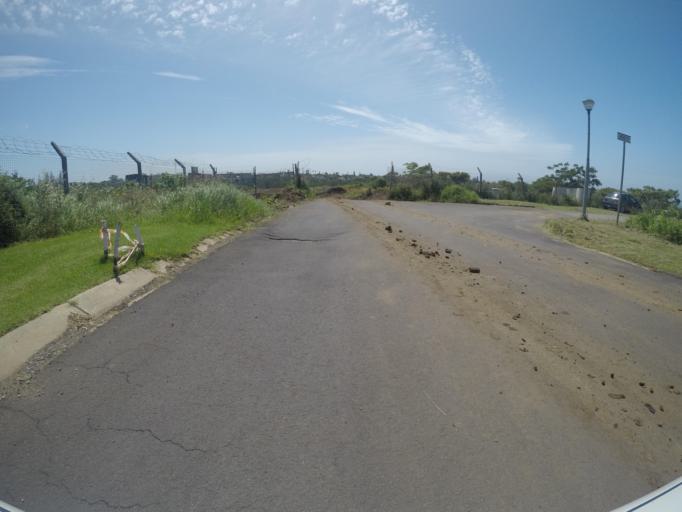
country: ZA
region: Eastern Cape
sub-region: Buffalo City Metropolitan Municipality
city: East London
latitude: -32.9403
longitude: 27.9977
